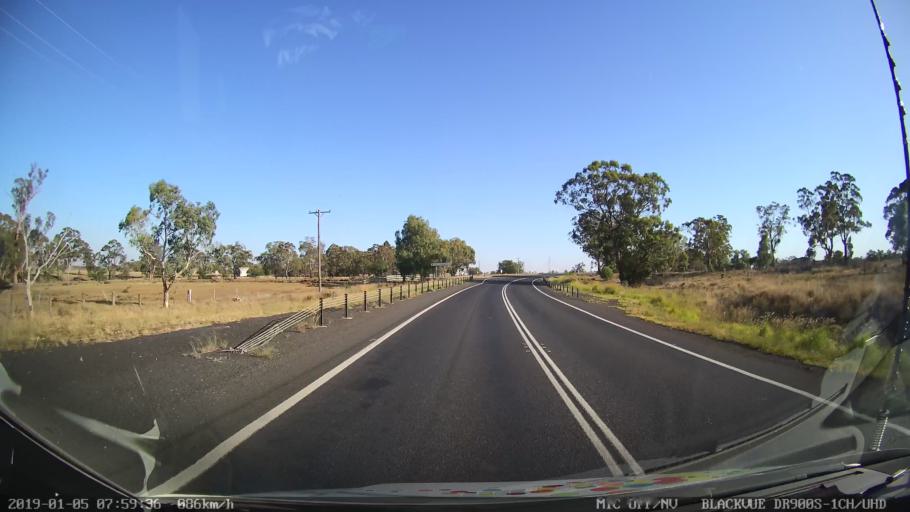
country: AU
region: New South Wales
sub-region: Gilgandra
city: Gilgandra
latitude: -31.7000
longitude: 148.6793
